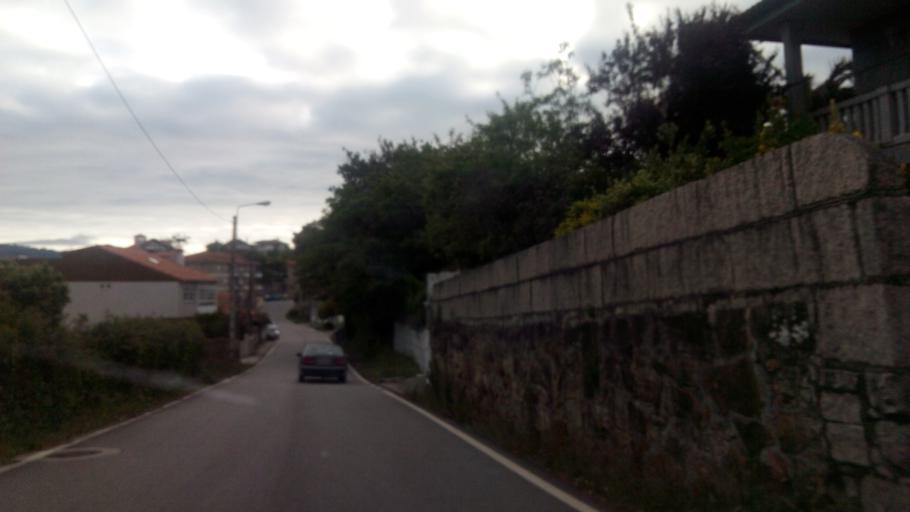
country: ES
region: Galicia
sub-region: Provincia de Pontevedra
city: Nigran
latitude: 42.1227
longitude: -8.8084
